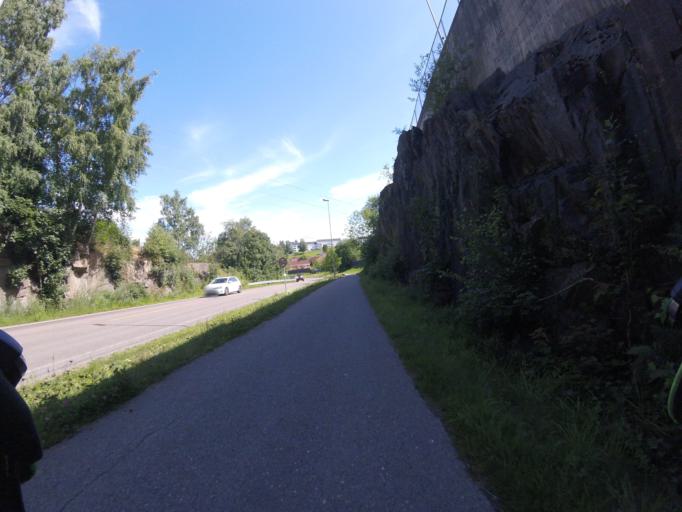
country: NO
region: Akershus
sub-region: Skedsmo
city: Lillestrom
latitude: 59.9522
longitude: 11.0212
